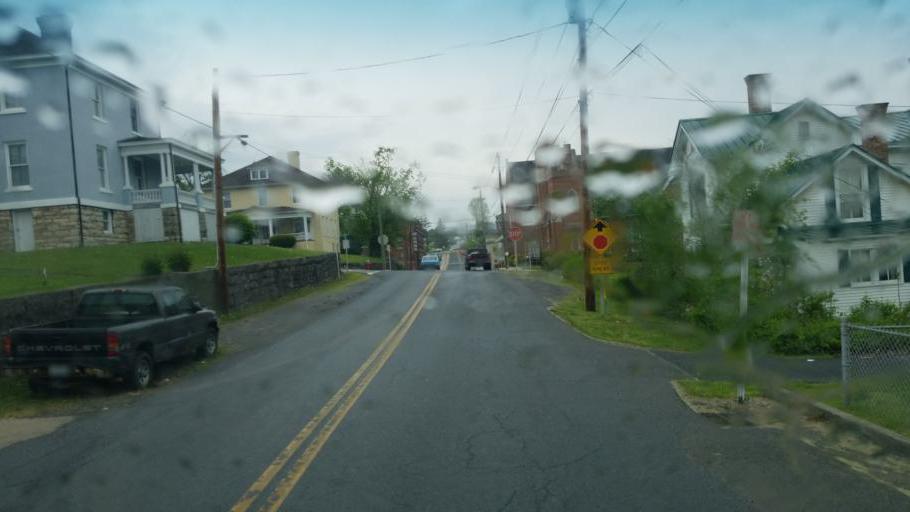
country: US
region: Virginia
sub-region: Smyth County
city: Marion
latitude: 36.8315
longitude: -81.5186
